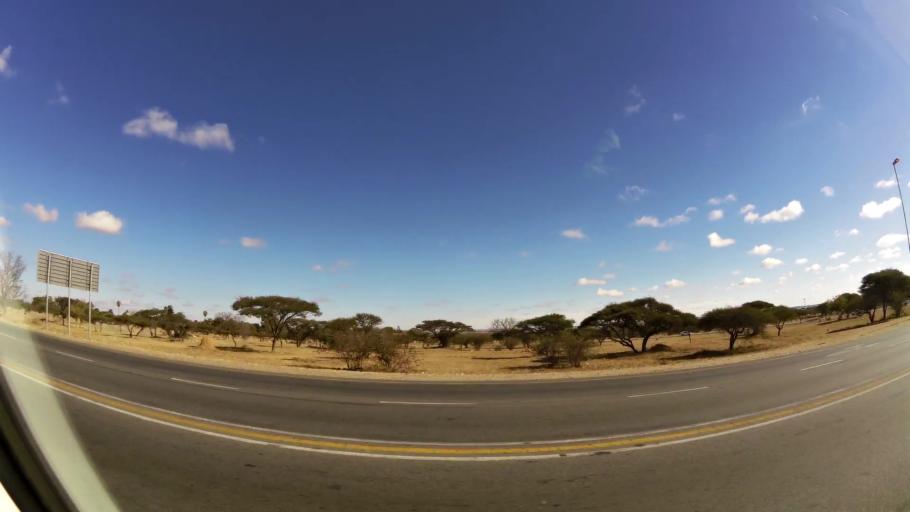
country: ZA
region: Limpopo
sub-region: Capricorn District Municipality
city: Polokwane
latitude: -23.8766
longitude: 29.4618
